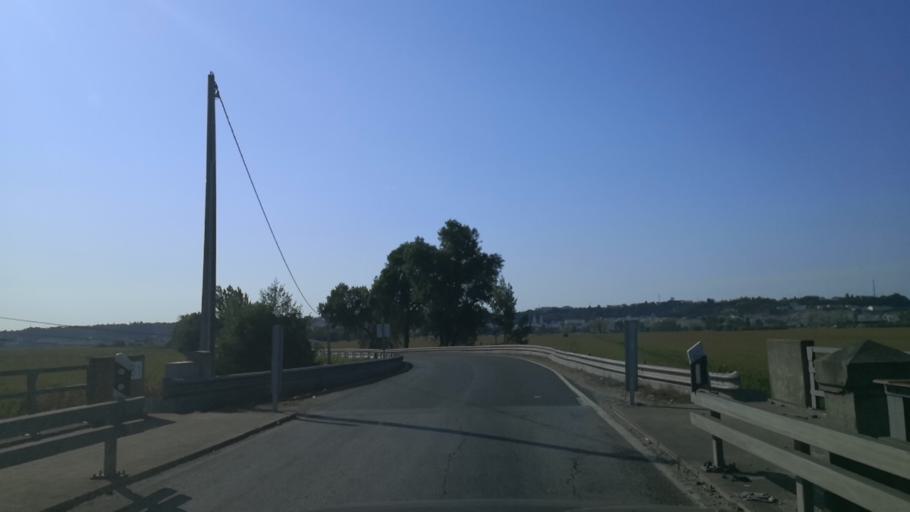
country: PT
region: Santarem
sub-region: Coruche
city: Coruche
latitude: 38.9520
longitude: -8.5113
